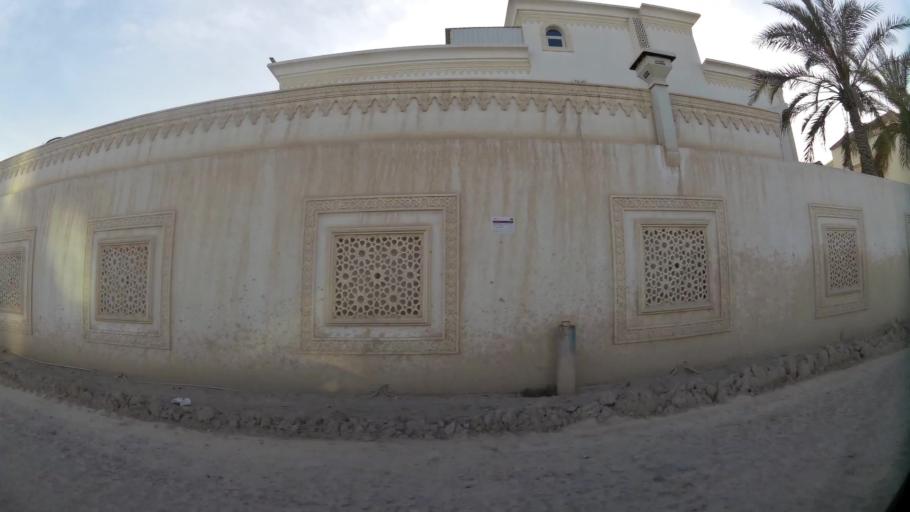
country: QA
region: Al Wakrah
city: Al Wakrah
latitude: 25.1440
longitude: 51.5956
